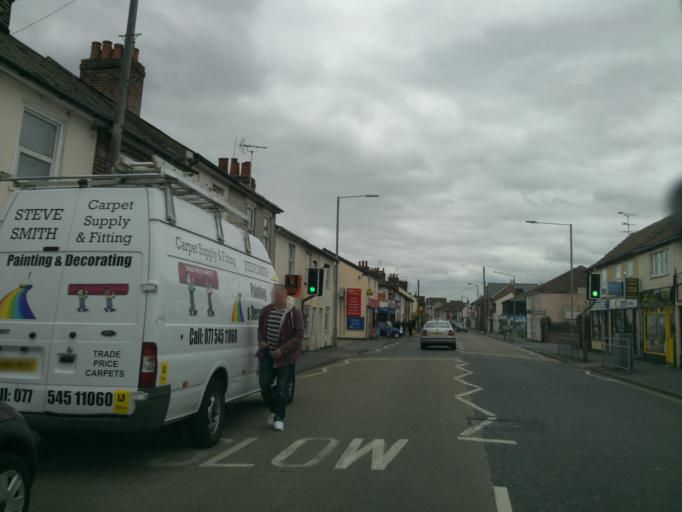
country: GB
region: England
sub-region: Essex
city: Colchester
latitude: 51.8849
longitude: 0.9174
